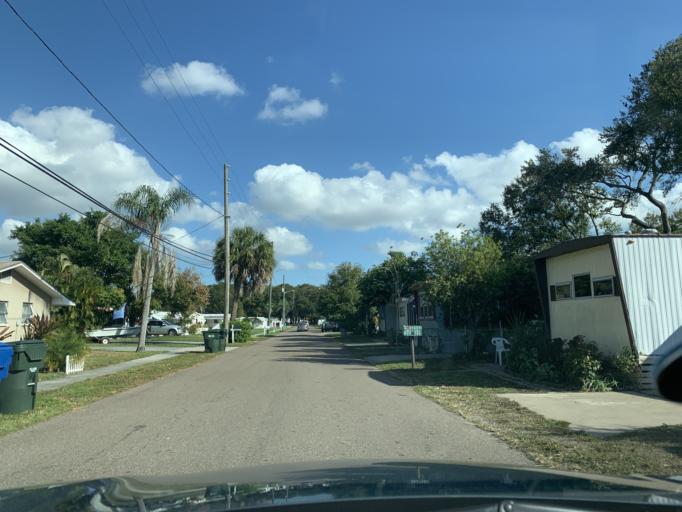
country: US
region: Florida
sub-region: Pinellas County
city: Largo
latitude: 27.9241
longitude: -82.7940
